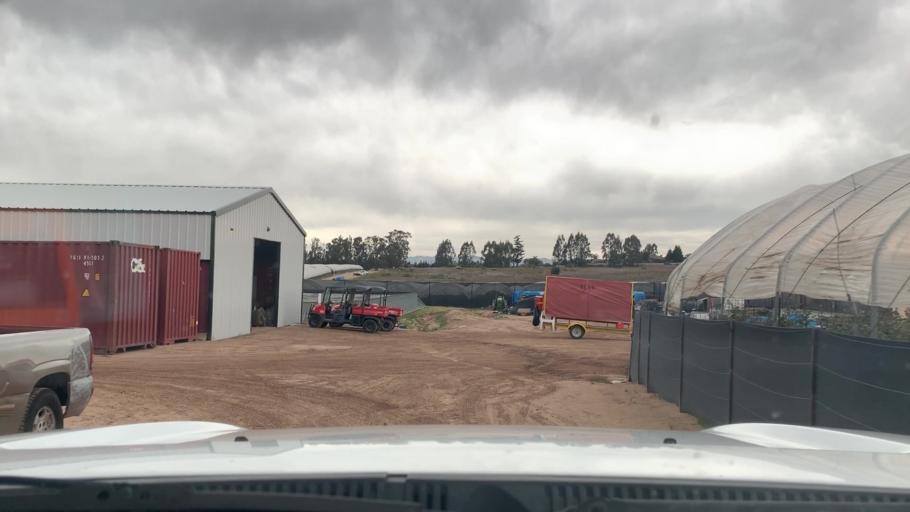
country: US
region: California
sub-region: San Luis Obispo County
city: Callender
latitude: 35.0620
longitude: -120.5668
